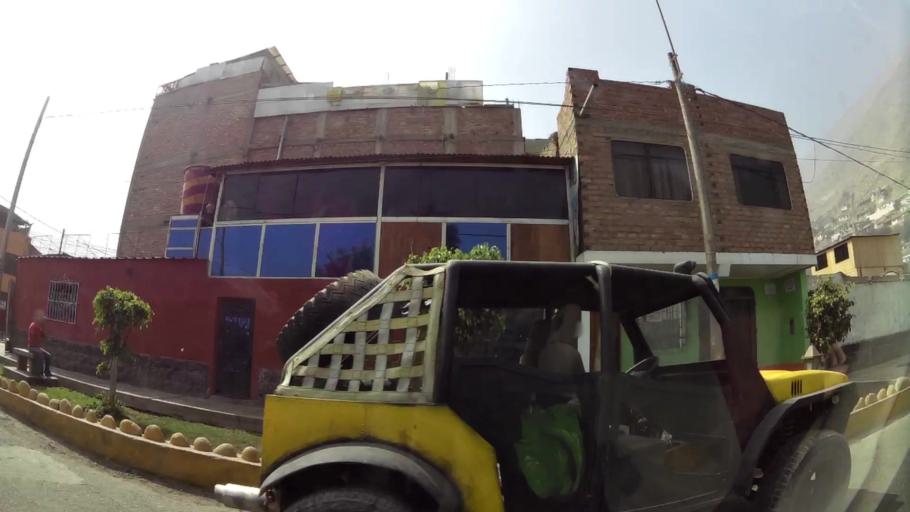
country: PE
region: Lima
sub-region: Lima
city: Asentamiento Humano Nicolas de Pierola
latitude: -11.9399
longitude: -76.6958
